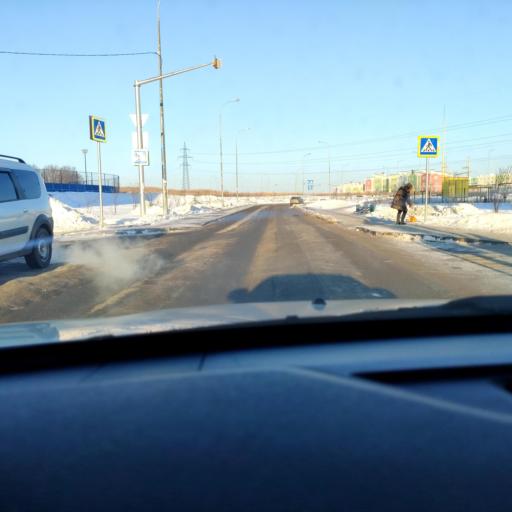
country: RU
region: Samara
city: Petra-Dubrava
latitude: 53.3043
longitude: 50.3365
